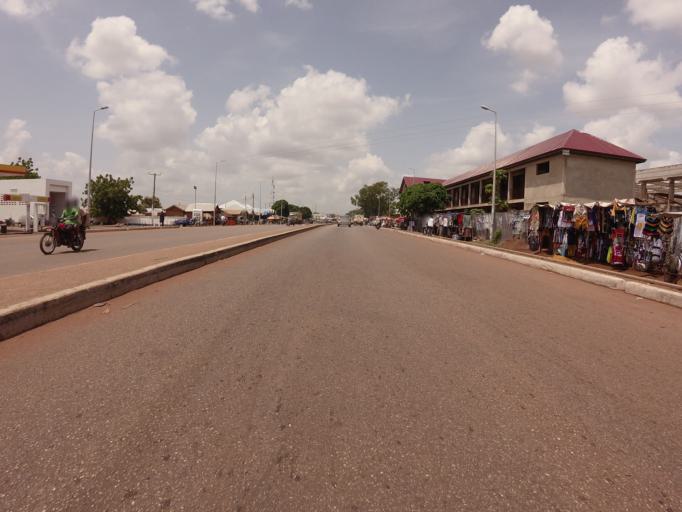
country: GH
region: Northern
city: Tamale
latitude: 9.4043
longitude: -0.8509
